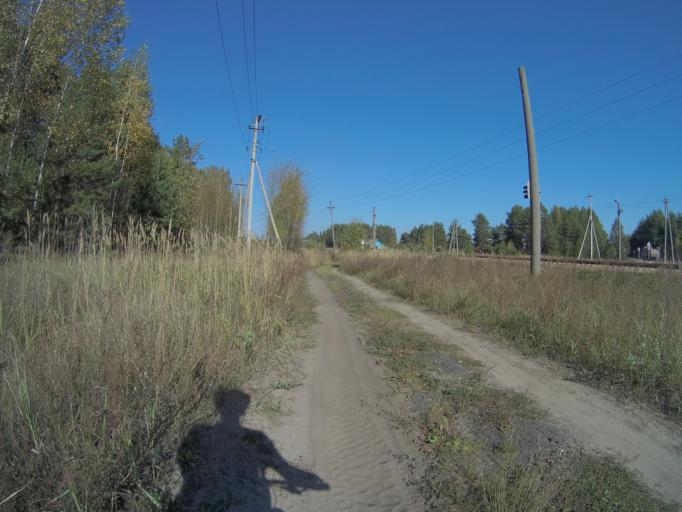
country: RU
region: Vladimir
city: Raduzhnyy
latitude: 56.0235
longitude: 40.3857
